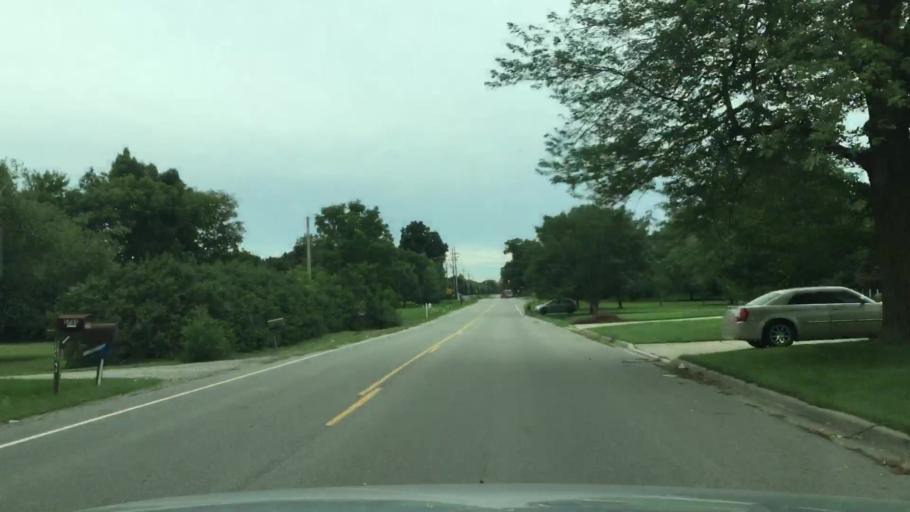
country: US
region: Michigan
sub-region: Washtenaw County
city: Ypsilanti
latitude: 42.2043
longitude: -83.6599
